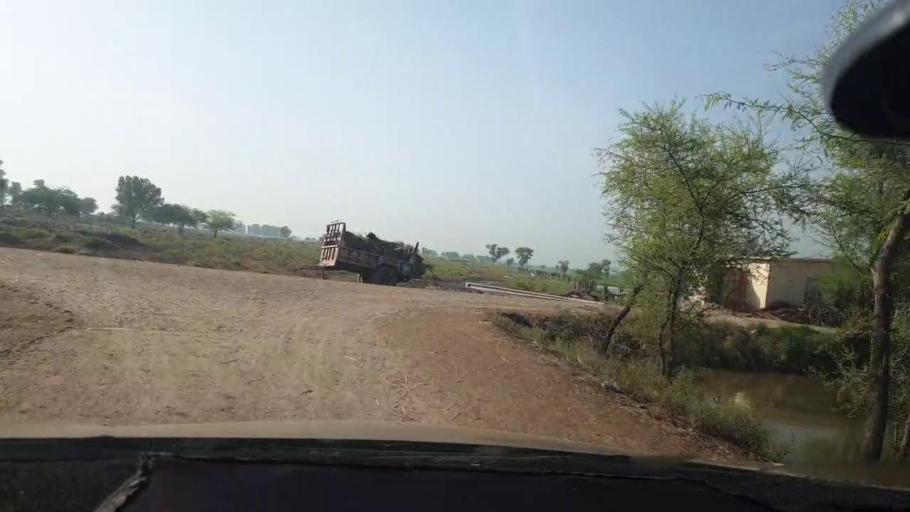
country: PK
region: Sindh
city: Kambar
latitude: 27.6446
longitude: 68.0421
